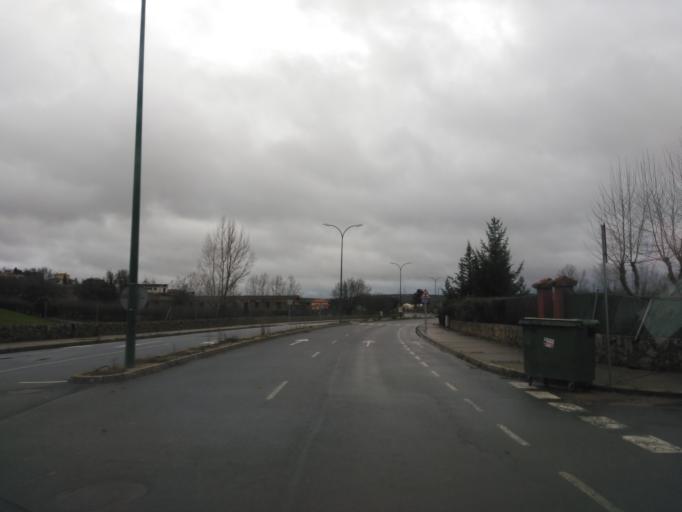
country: ES
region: Castille and Leon
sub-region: Provincia de Salamanca
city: Villamayor
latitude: 40.9823
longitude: -5.7131
